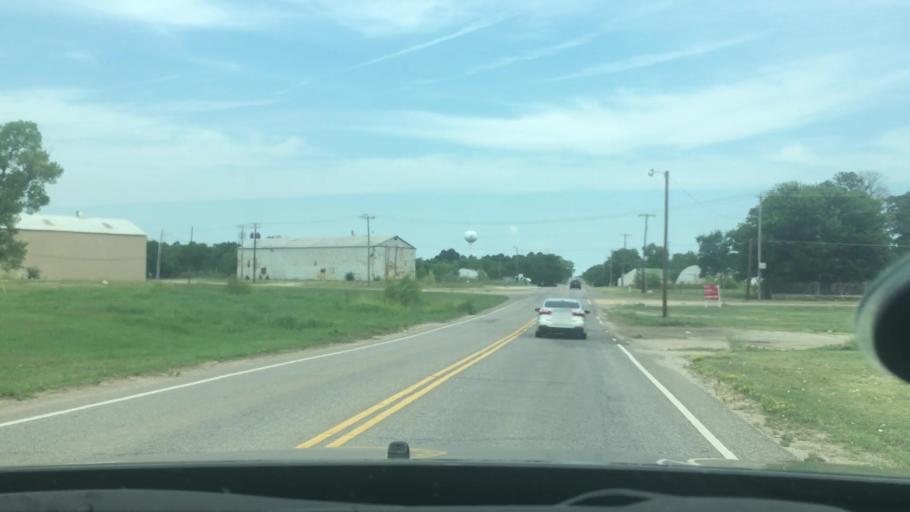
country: US
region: Oklahoma
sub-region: Seminole County
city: Seminole
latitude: 35.2312
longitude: -96.6859
